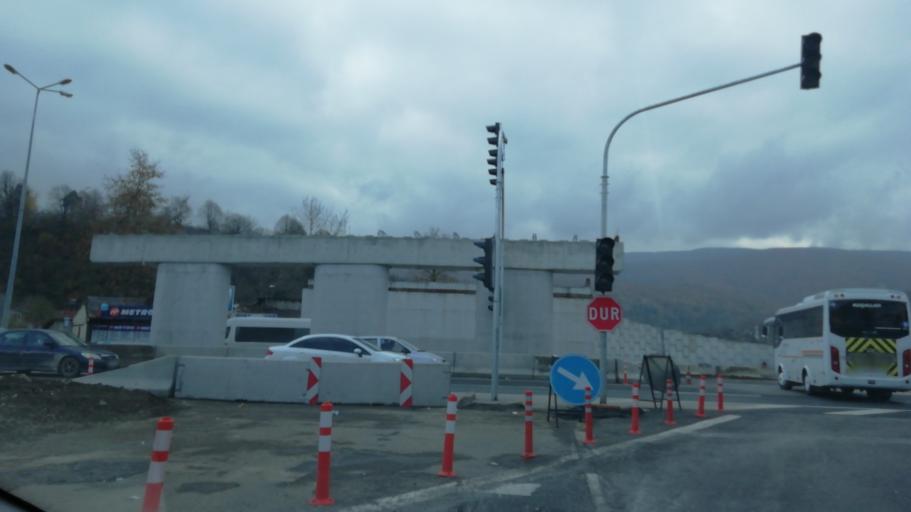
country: TR
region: Duzce
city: Kaynasli
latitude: 40.7823
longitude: 31.2772
